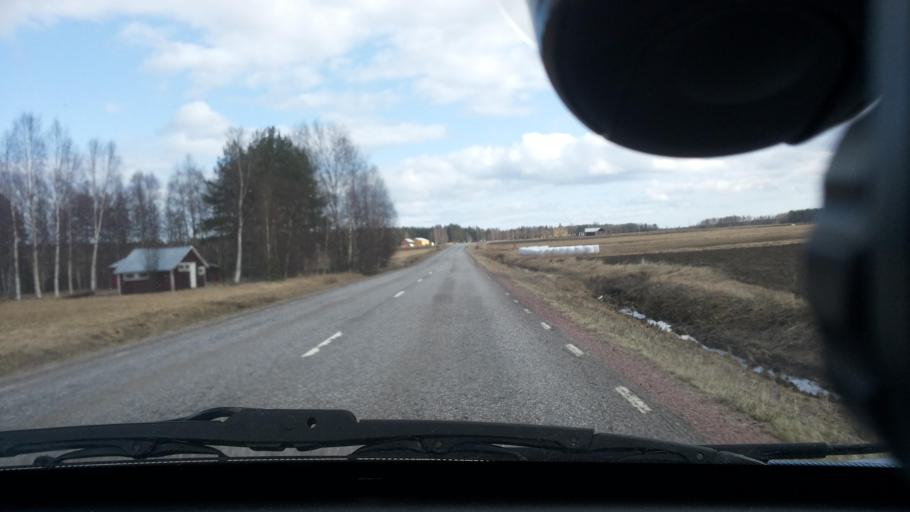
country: SE
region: Norrbotten
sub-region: Lulea Kommun
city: Sodra Sunderbyn
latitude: 65.6540
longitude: 21.8560
